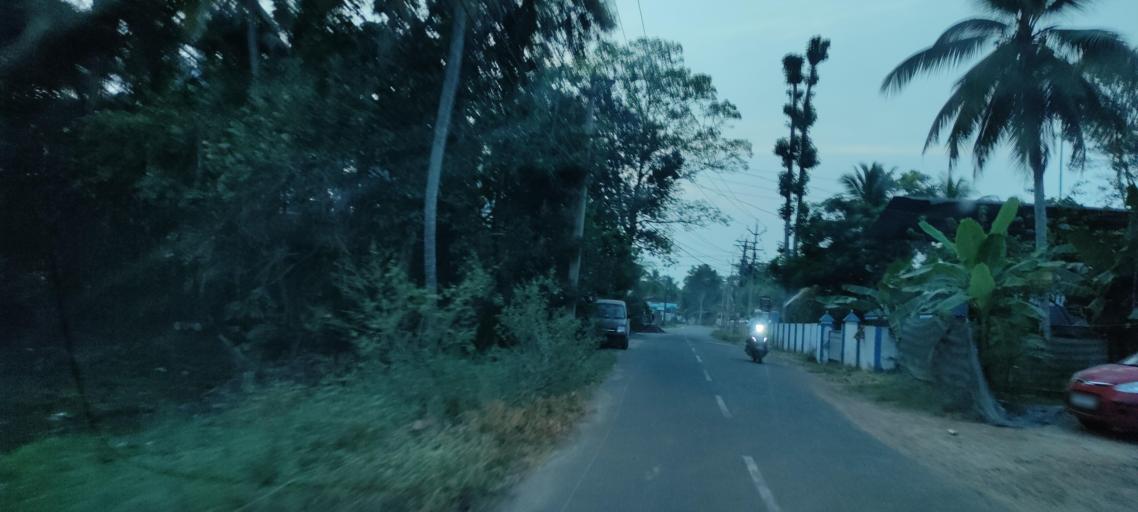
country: IN
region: Kerala
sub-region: Pattanamtitta
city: Tiruvalla
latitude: 9.3311
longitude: 76.5096
